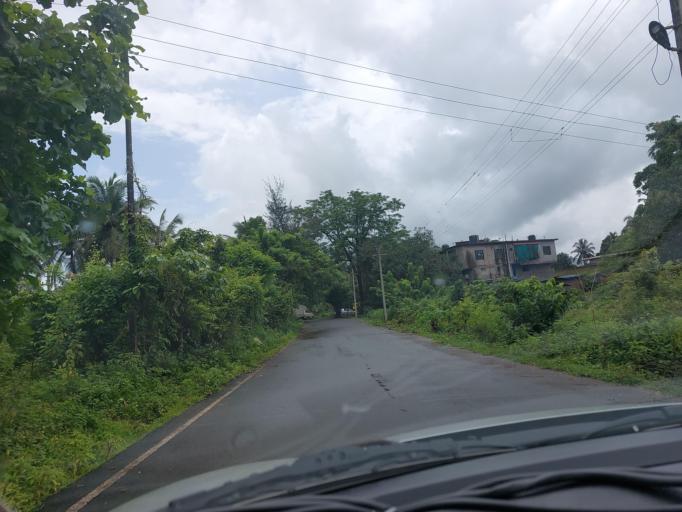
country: IN
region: Goa
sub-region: North Goa
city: Valpoy
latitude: 15.5386
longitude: 74.1383
